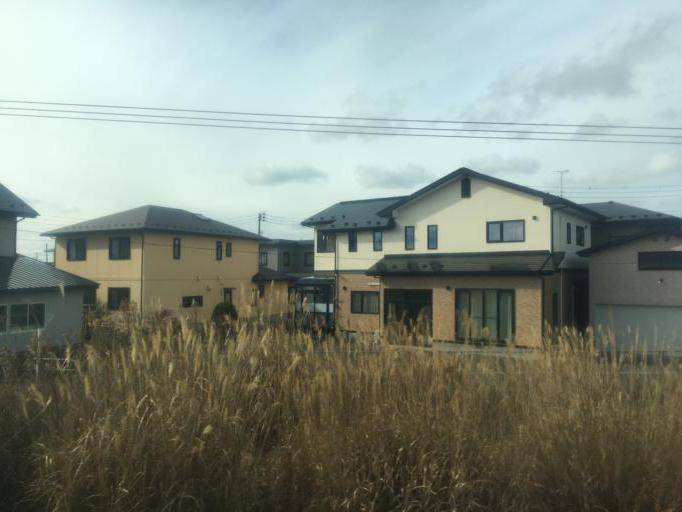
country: JP
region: Akita
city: Tenno
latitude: 39.9454
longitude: 140.0791
